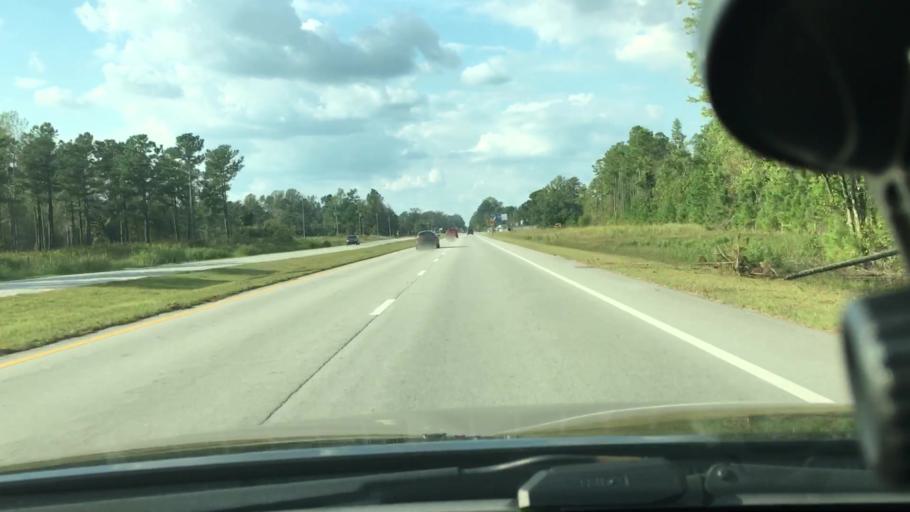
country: US
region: North Carolina
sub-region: Craven County
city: New Bern
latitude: 35.1493
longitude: -77.0332
